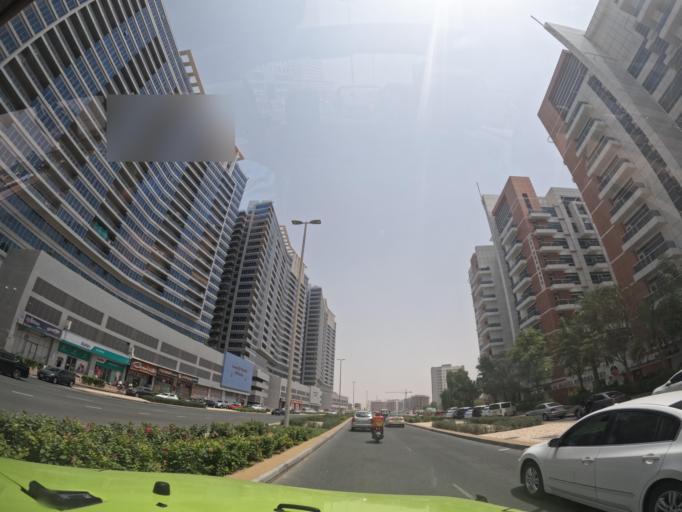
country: AE
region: Dubai
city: Dubai
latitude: 25.0920
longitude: 55.3841
